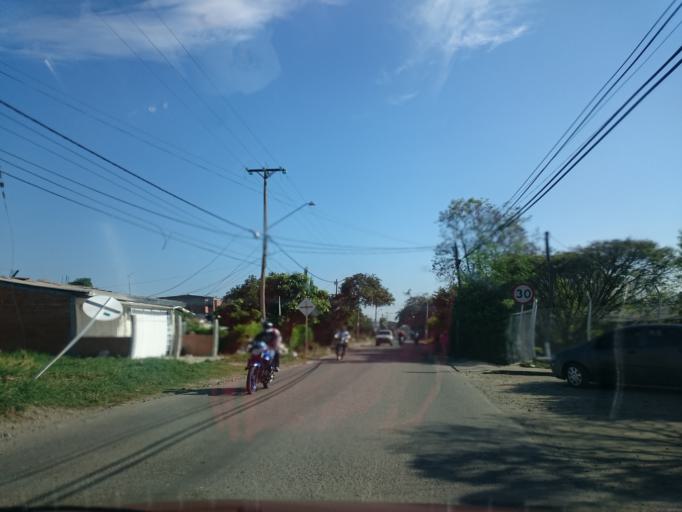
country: CO
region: Cauca
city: Santander de Quilichao
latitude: 3.0213
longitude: -76.4789
